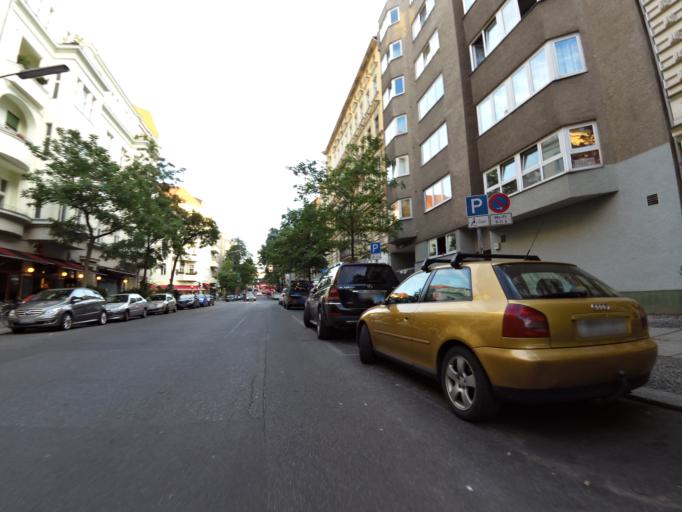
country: DE
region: Berlin
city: Berlin Schoeneberg
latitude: 52.4880
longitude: 13.3542
